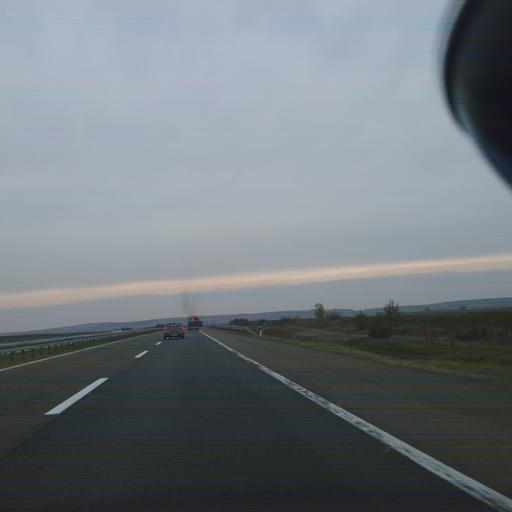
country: RS
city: Krcedin
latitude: 45.1087
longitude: 20.1052
